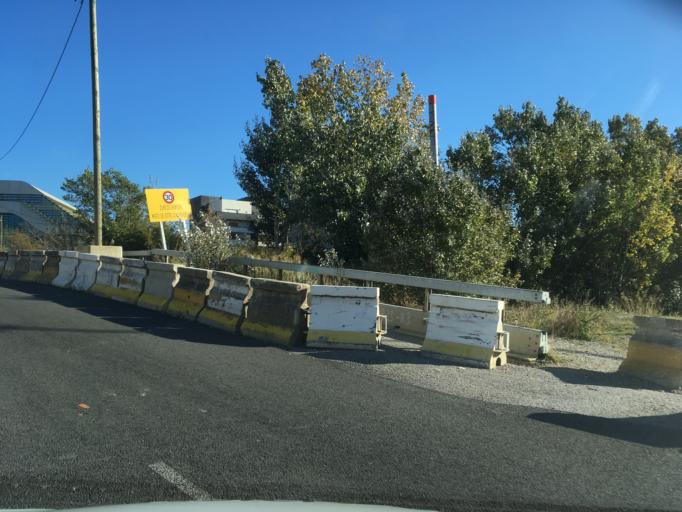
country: FR
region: Languedoc-Roussillon
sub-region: Departement de l'Herault
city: Juvignac
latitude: 43.6246
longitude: 3.8207
